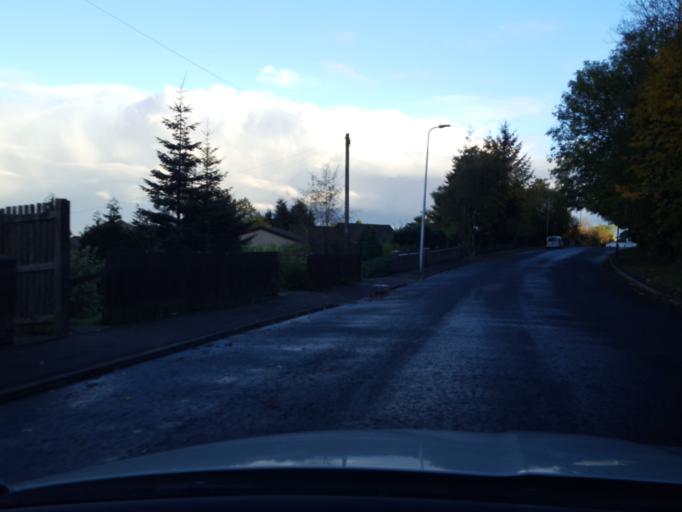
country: GB
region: Scotland
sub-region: Dundee City
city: Dundee
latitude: 56.4719
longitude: -2.9862
